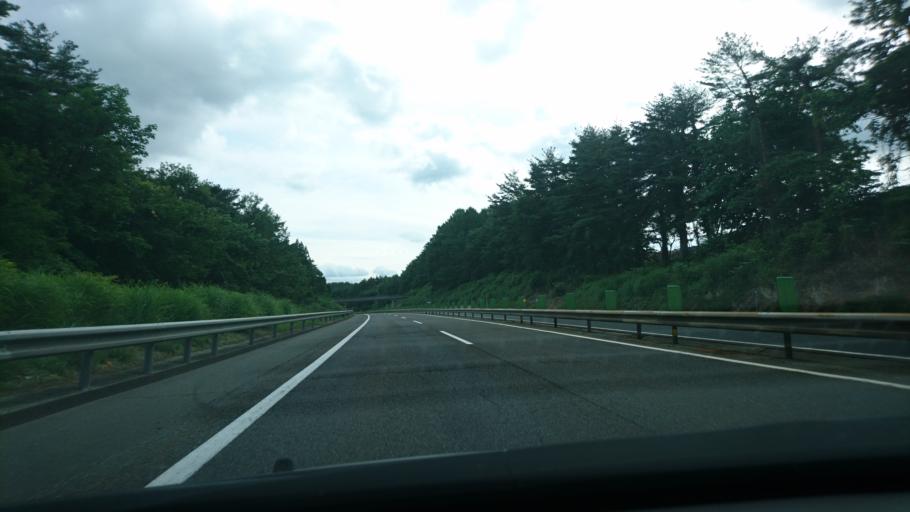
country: JP
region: Aomori
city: Hachinohe
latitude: 40.4313
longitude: 141.4426
